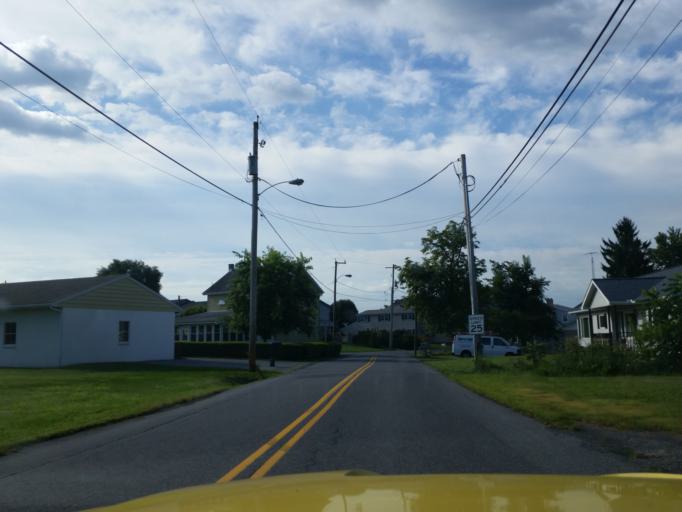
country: US
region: Pennsylvania
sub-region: Lebanon County
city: Fredericksburg
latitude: 40.4487
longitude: -76.4323
